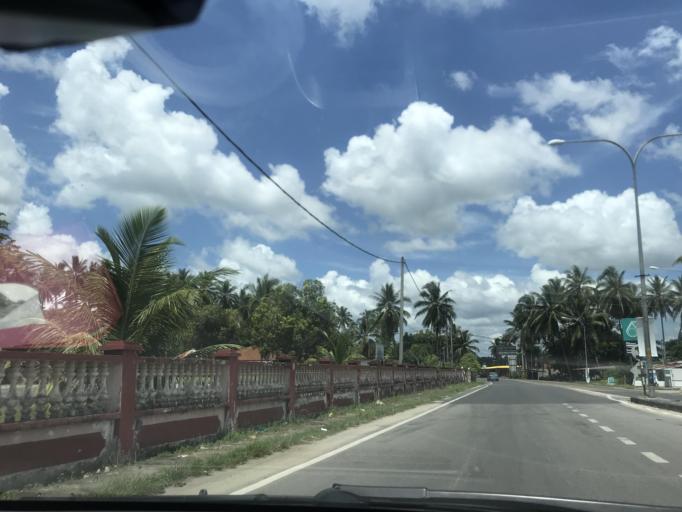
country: MY
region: Kelantan
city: Tumpat
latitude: 6.2156
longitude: 102.1110
